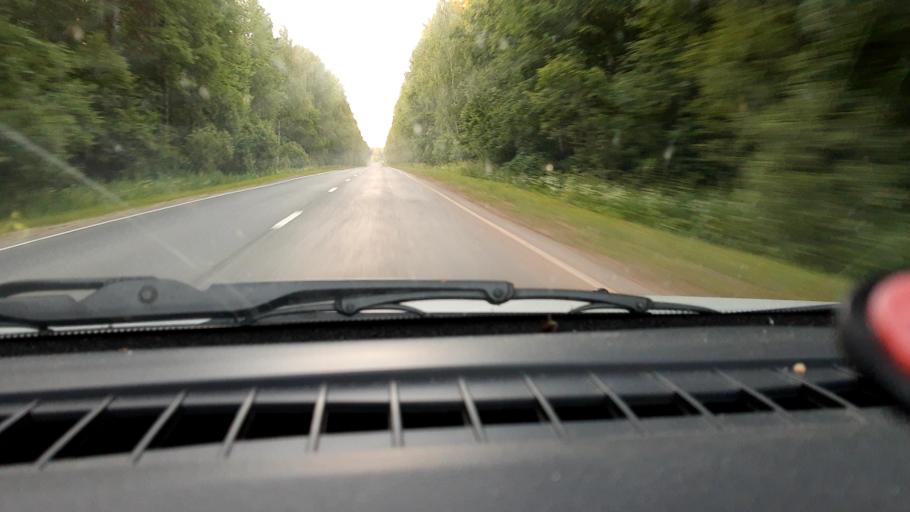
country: RU
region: Nizjnij Novgorod
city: Uren'
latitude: 57.2834
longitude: 45.6409
